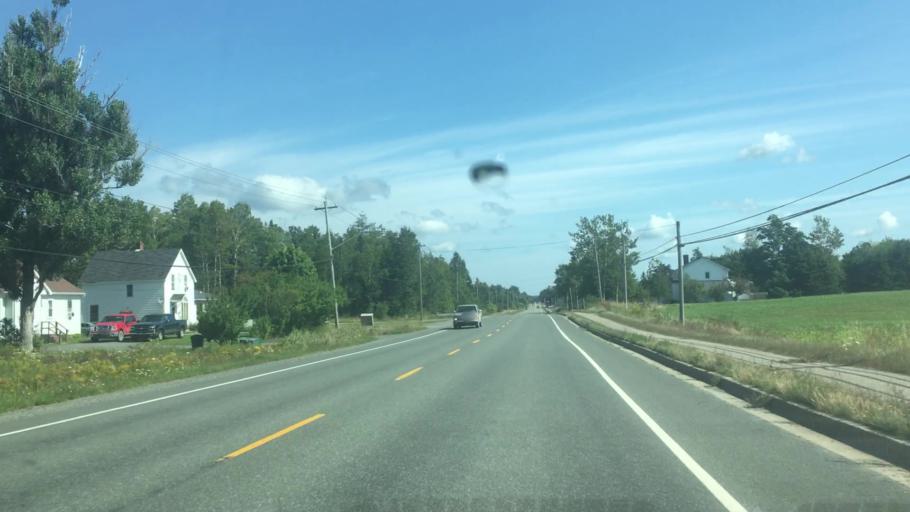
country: CA
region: Nova Scotia
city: Sydney
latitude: 46.0548
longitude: -60.3139
